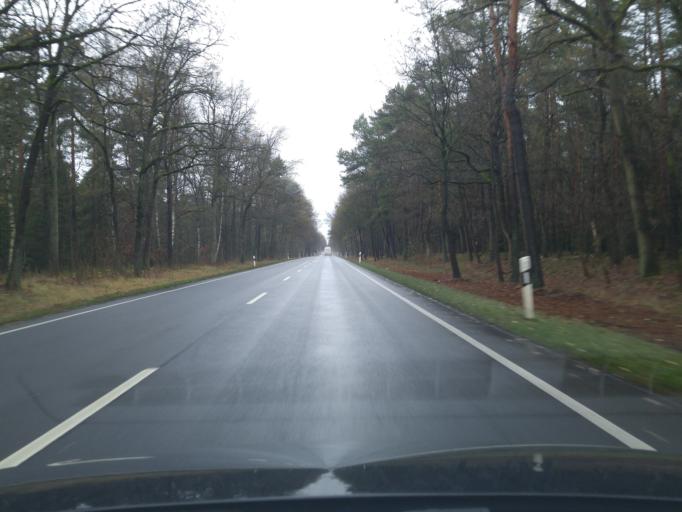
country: DE
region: Lower Saxony
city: Gross Oesingen
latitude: 52.6811
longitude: 10.4713
